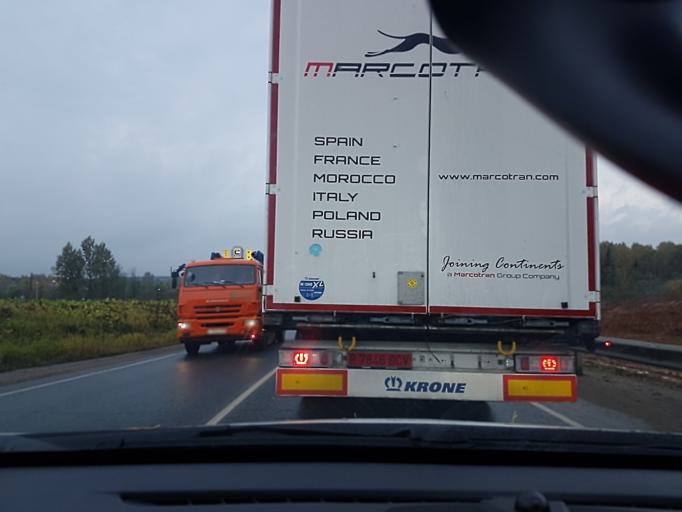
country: RU
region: Moskovskaya
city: Snegiri
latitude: 55.9323
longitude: 36.9544
